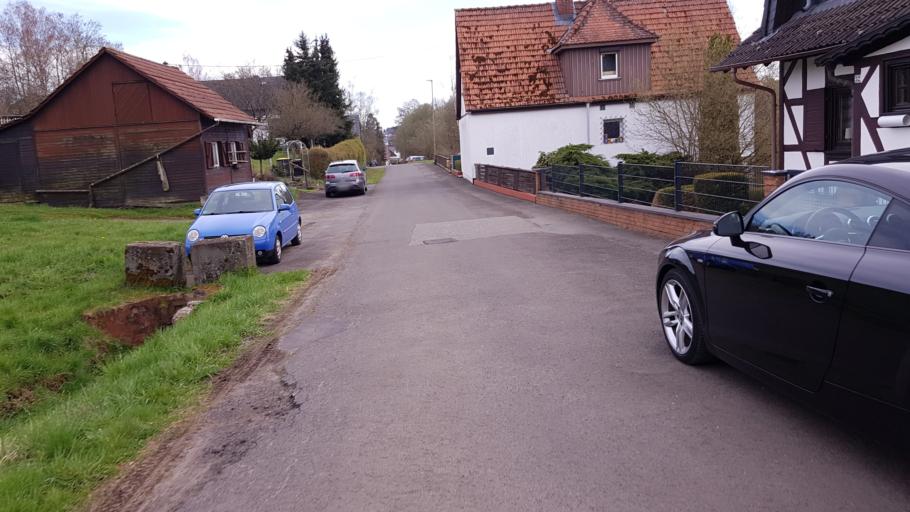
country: DE
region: Hesse
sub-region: Regierungsbezirk Giessen
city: Homberg
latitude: 50.6546
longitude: 9.0356
